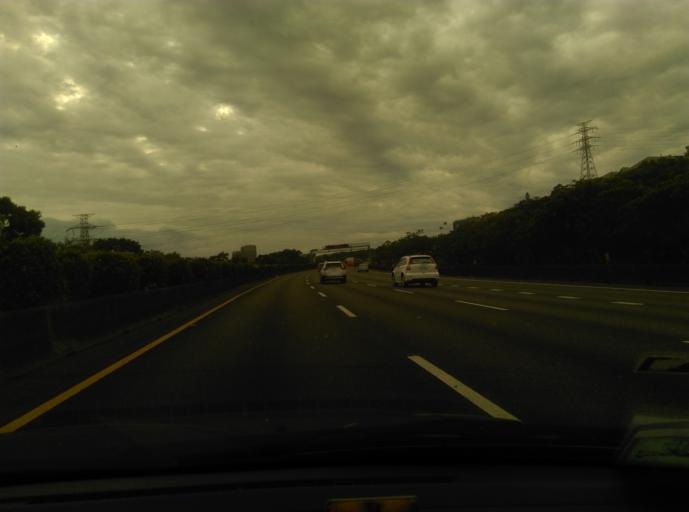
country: TW
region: Taiwan
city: Daxi
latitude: 24.9131
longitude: 121.2932
